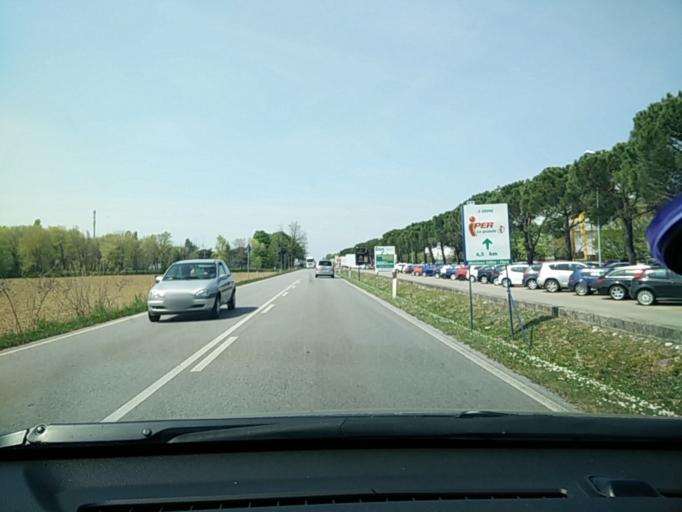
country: IT
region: Friuli Venezia Giulia
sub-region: Provincia di Udine
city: Buttrio
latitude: 46.0011
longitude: 13.3452
